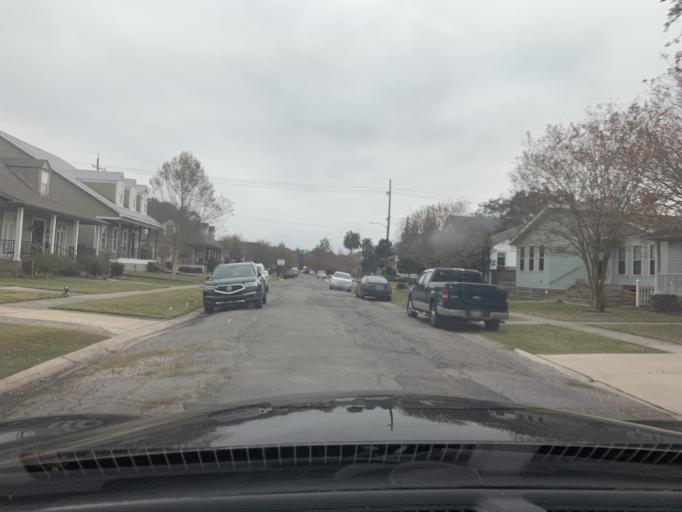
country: US
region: Louisiana
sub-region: Jefferson Parish
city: Metairie
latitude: 30.0162
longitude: -90.1044
